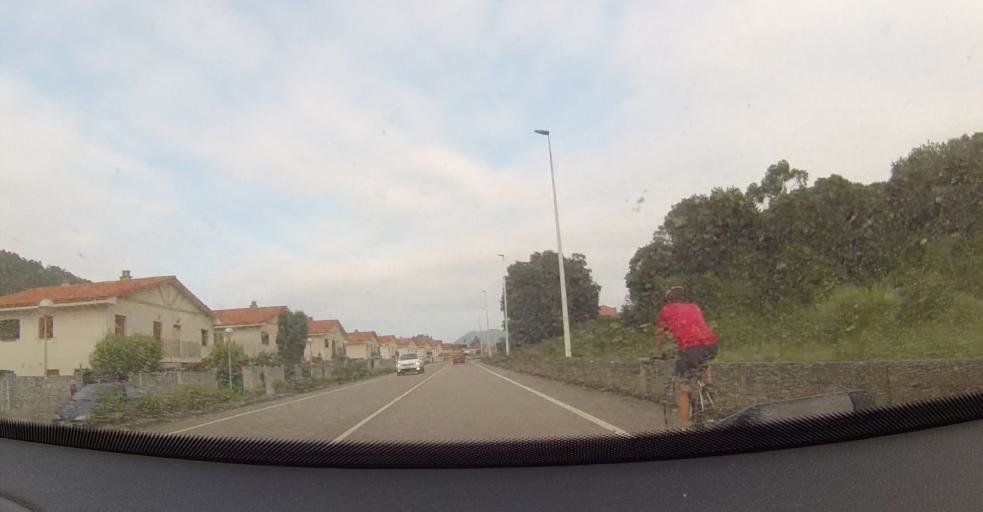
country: ES
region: Cantabria
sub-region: Provincia de Cantabria
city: Argonos
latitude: 43.4597
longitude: -3.5113
